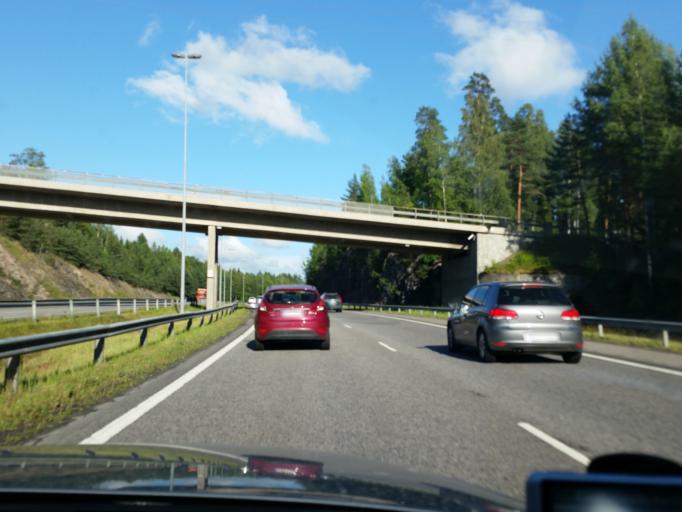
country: FI
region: Uusimaa
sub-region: Helsinki
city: Vihti
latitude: 60.2892
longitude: 24.4049
